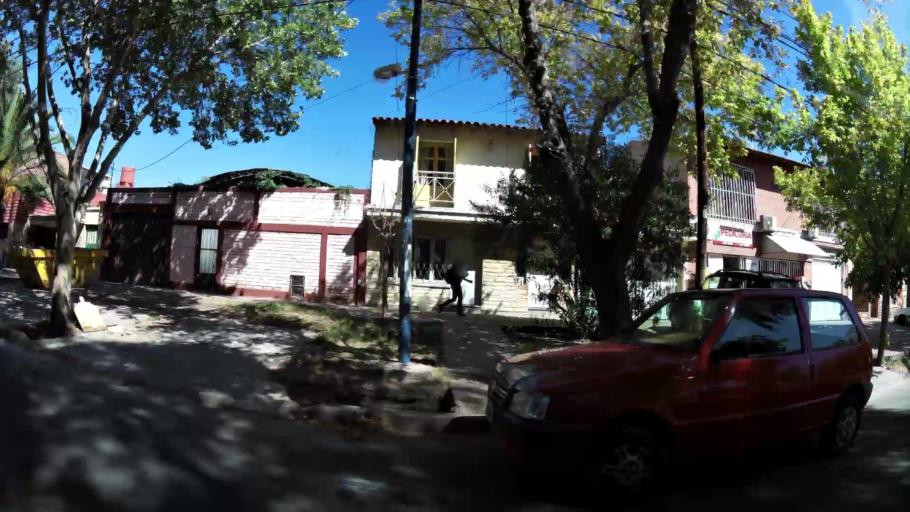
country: AR
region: Mendoza
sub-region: Departamento de Godoy Cruz
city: Godoy Cruz
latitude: -32.9190
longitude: -68.8595
